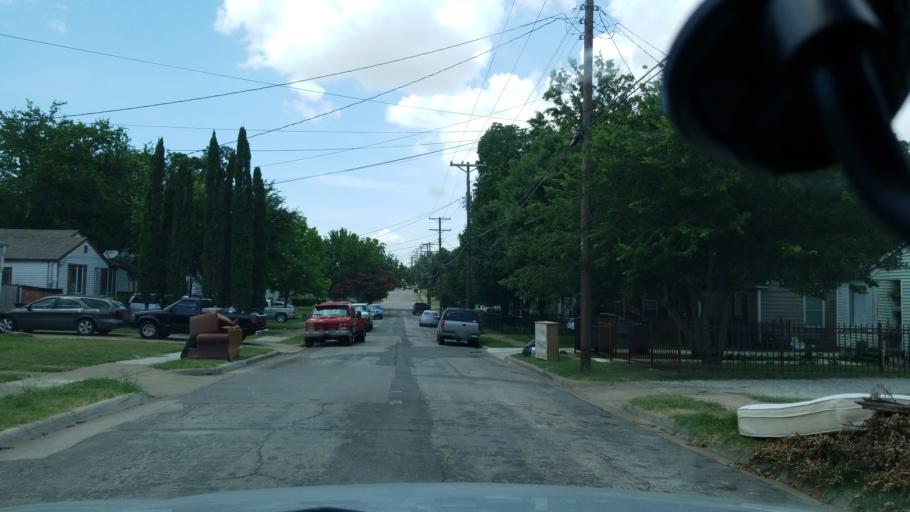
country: US
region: Texas
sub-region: Dallas County
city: Cockrell Hill
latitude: 32.7319
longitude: -96.8815
